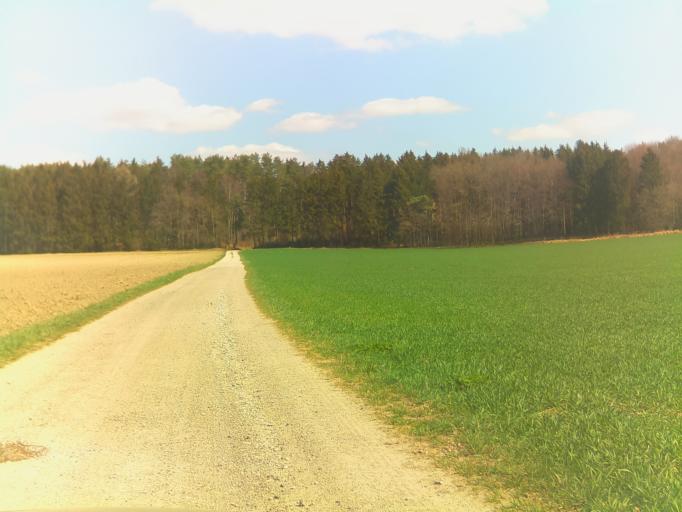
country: DE
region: Bavaria
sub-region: Swabia
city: Aichach
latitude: 48.4872
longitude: 11.1484
